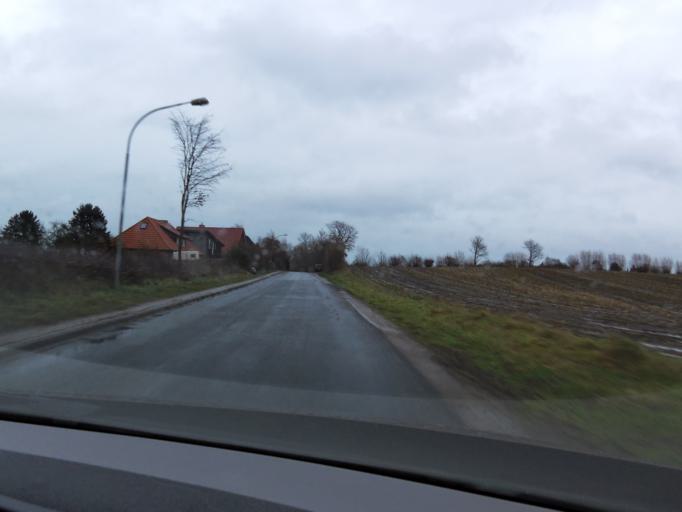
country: DE
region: Schleswig-Holstein
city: Mustin
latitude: 53.6865
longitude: 10.8772
